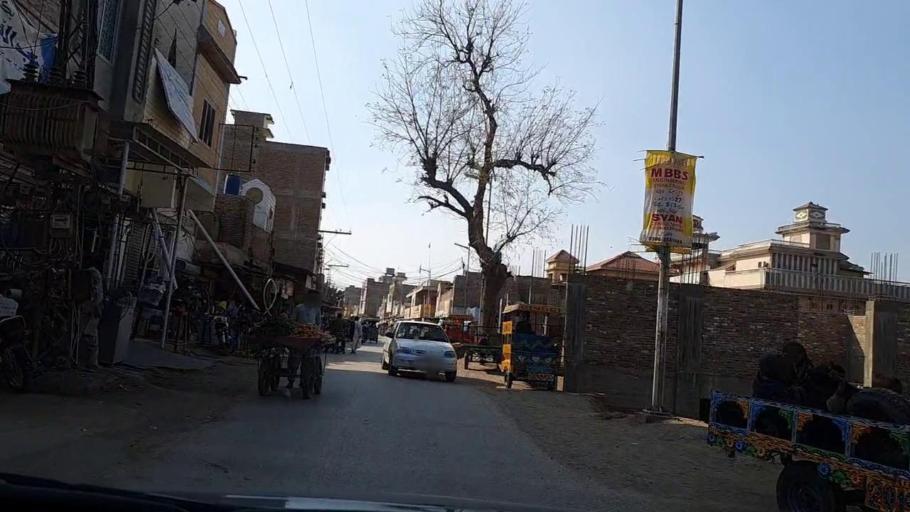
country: PK
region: Sindh
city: Sakrand
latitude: 26.1360
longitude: 68.2730
